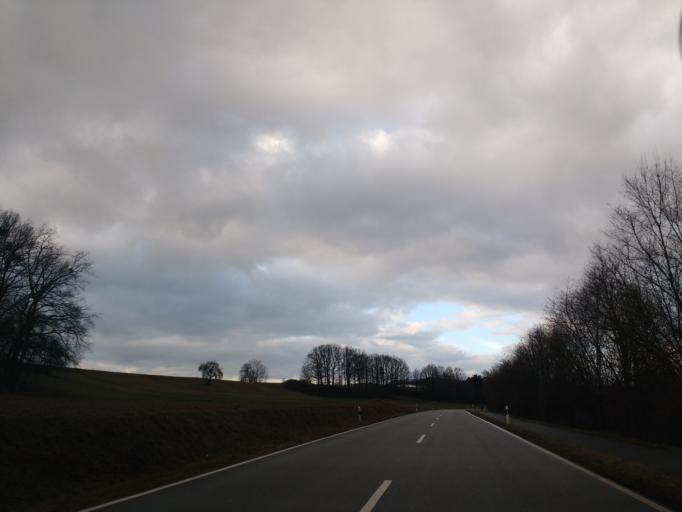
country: DE
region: Bavaria
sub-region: Regierungsbezirk Mittelfranken
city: Herzogenaurach
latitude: 49.5788
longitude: 10.8625
